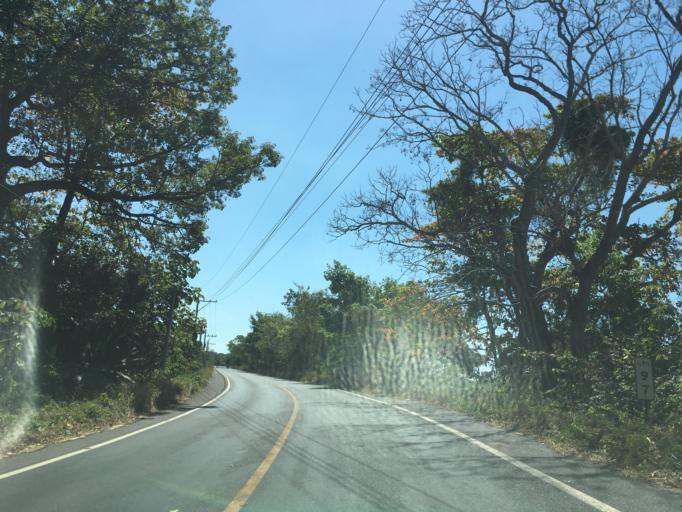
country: GT
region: Escuintla
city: Puerto San Jose
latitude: 13.9834
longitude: -90.8927
